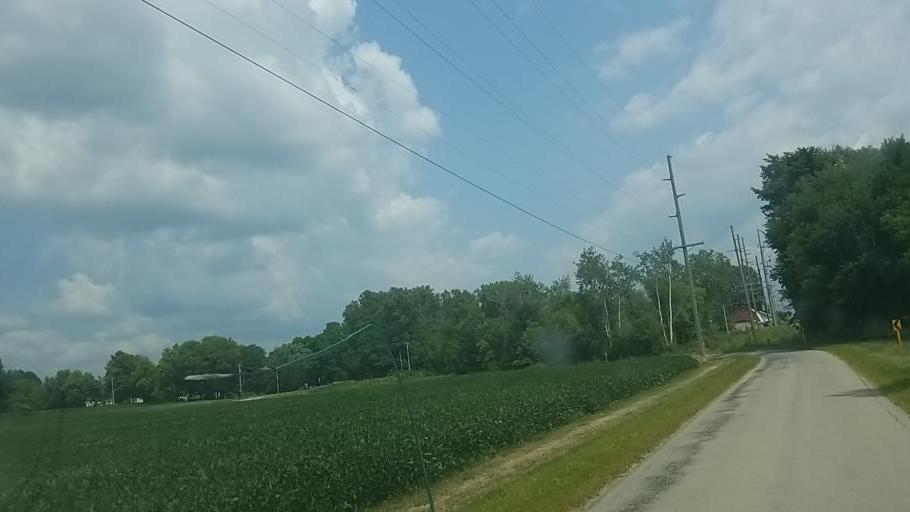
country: US
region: Ohio
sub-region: Crawford County
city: Bucyrus
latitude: 40.8337
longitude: -83.1145
